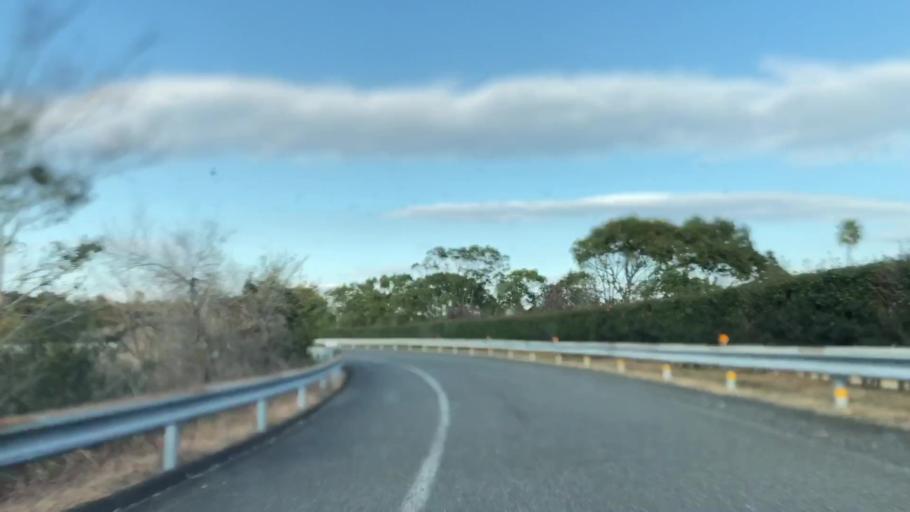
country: JP
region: Miyazaki
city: Miyazaki-shi
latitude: 31.8701
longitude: 131.4143
